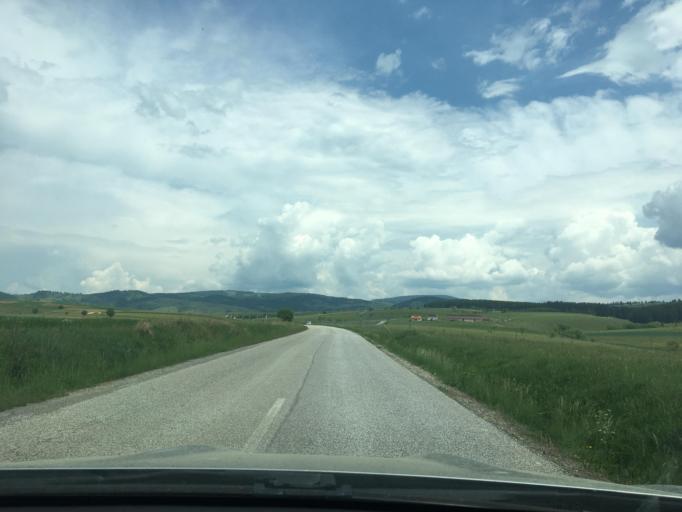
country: RO
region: Harghita
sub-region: Comuna Ditrau
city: Ditrau
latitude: 46.8392
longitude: 25.4964
